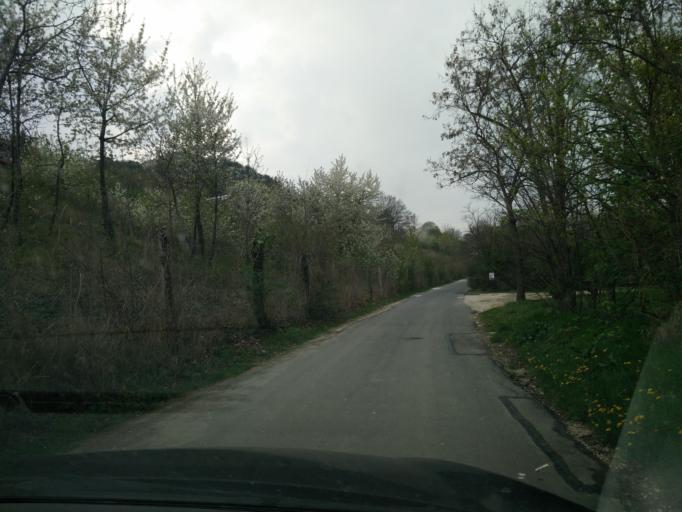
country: HU
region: Pest
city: Budaors
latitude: 47.4645
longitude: 18.9381
